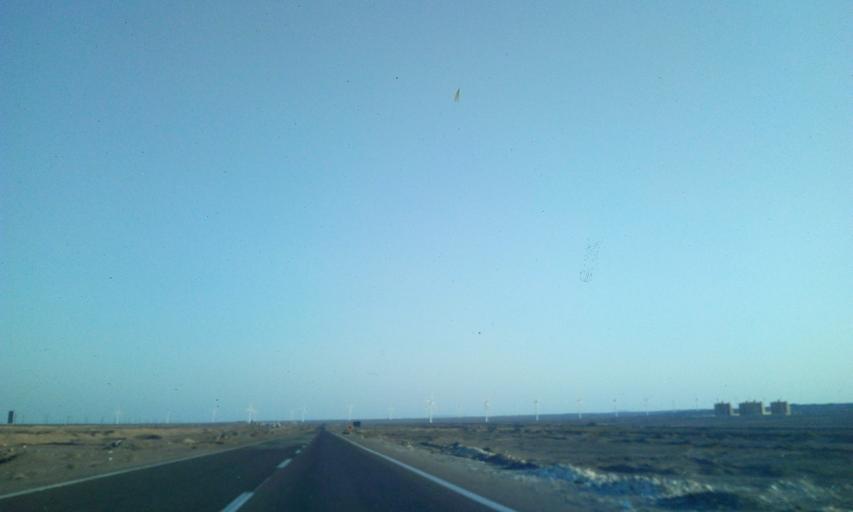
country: EG
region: South Sinai
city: Tor
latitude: 28.0960
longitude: 33.2538
